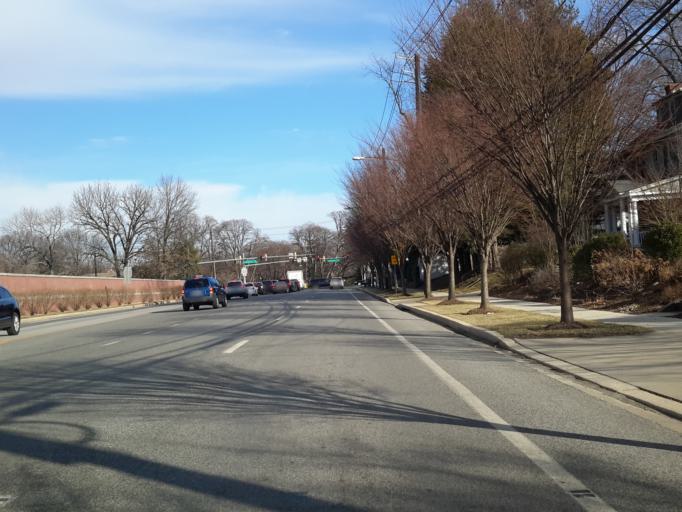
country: US
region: Maryland
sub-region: Montgomery County
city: Chevy Chase
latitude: 38.9878
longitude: -77.0790
